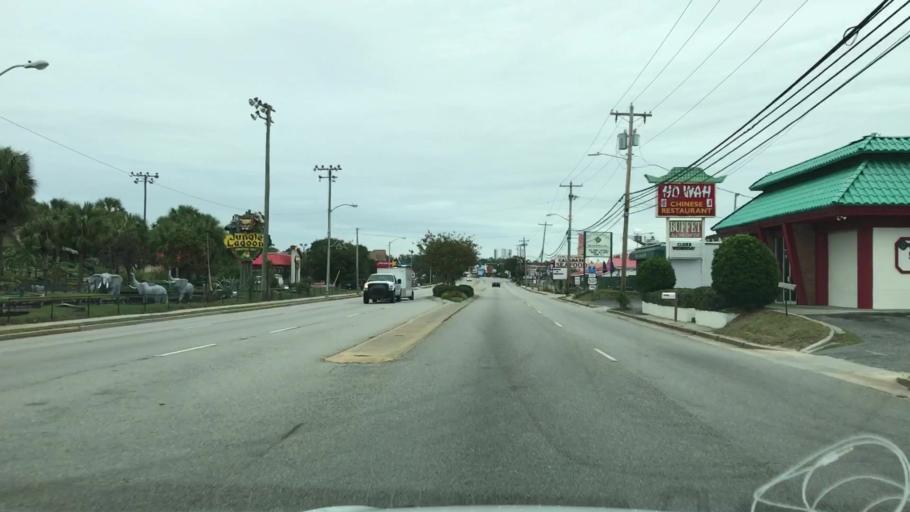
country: US
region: South Carolina
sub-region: Horry County
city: Myrtle Beach
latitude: 33.6825
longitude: -78.8945
